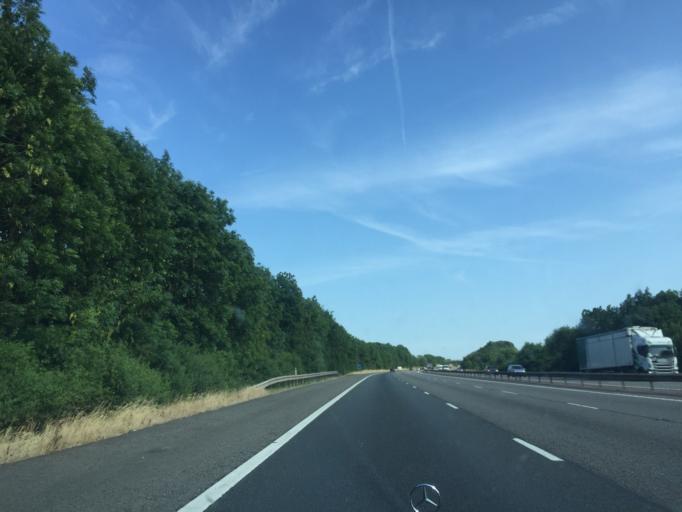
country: GB
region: England
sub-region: Warwickshire
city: Harbury
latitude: 52.1622
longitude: -1.4323
